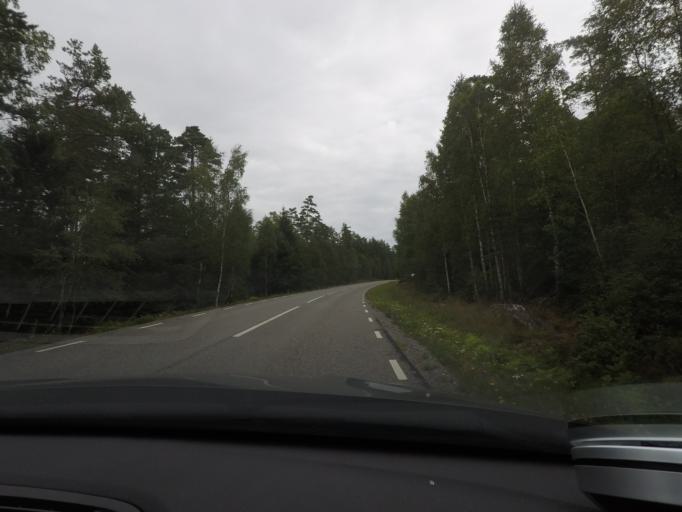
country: SE
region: Blekinge
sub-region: Olofstroms Kommun
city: Olofstroem
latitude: 56.4411
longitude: 14.4990
